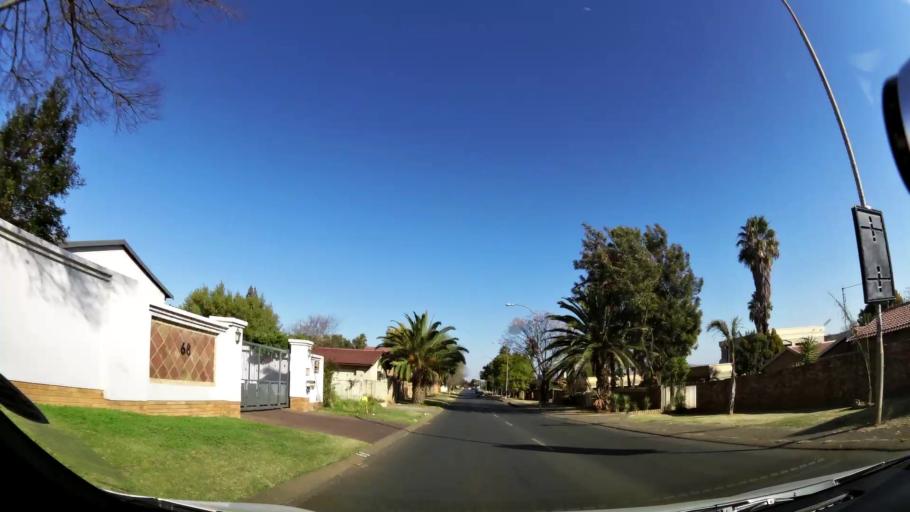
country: ZA
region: Gauteng
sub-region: City of Johannesburg Metropolitan Municipality
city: Johannesburg
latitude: -26.2934
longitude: 28.0539
